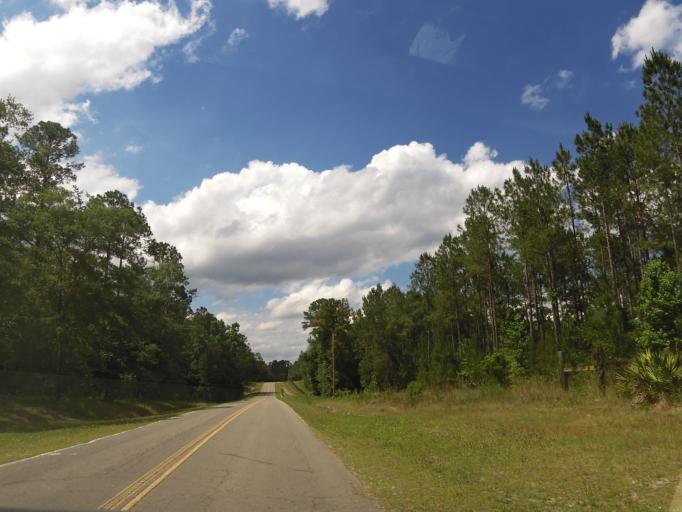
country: US
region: Florida
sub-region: Clay County
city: Asbury Lake
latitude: 29.9012
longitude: -81.8765
